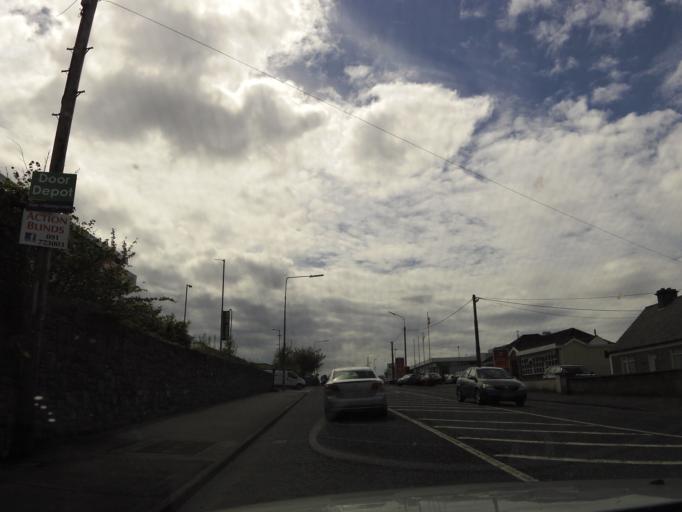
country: IE
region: Connaught
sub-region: County Galway
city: Gaillimh
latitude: 53.2944
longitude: -9.0164
